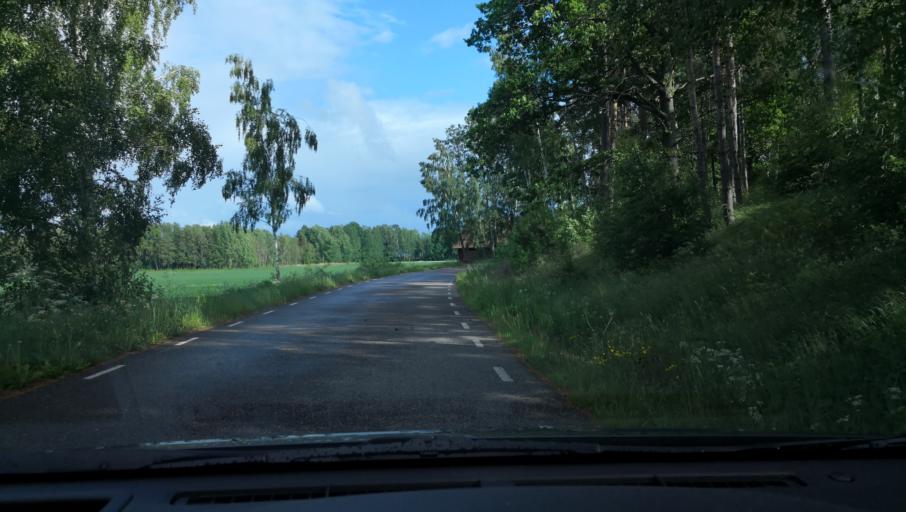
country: SE
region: OErebro
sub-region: Lindesbergs Kommun
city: Fellingsbro
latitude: 59.3089
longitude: 15.6796
